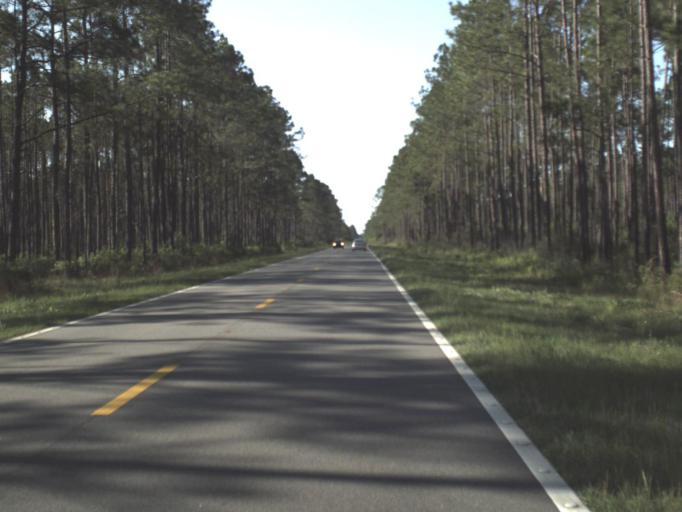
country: US
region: Florida
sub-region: Gulf County
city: Wewahitchka
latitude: 30.0978
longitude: -84.9852
